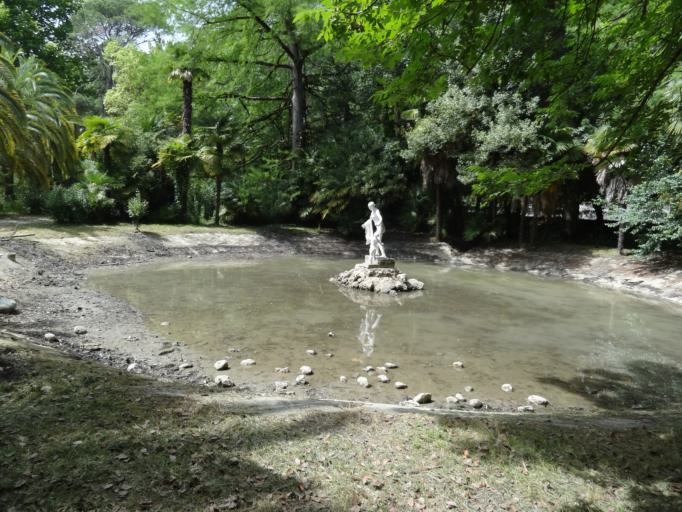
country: GE
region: Abkhazia
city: Gagra
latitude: 43.3235
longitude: 40.2295
